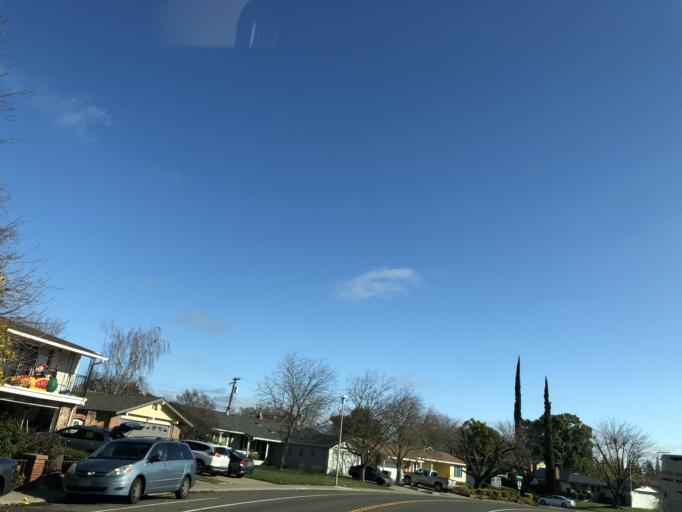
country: US
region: California
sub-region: Sacramento County
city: Rosemont
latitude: 38.5552
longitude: -121.3826
